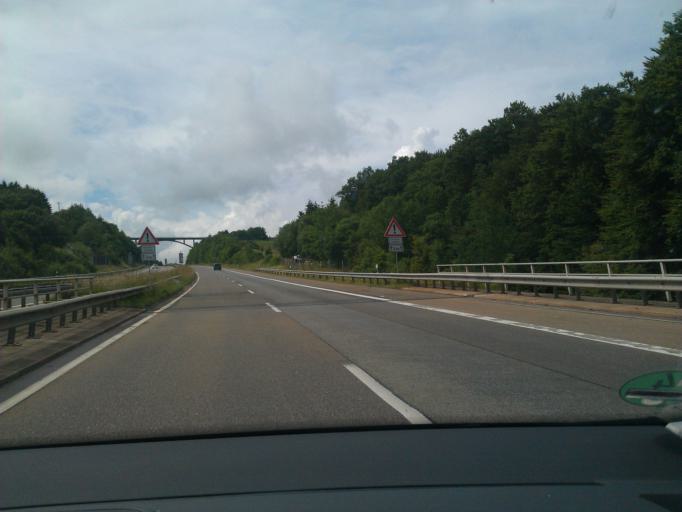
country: DE
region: Rheinland-Pfalz
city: Heisdorf
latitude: 50.1288
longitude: 6.4238
